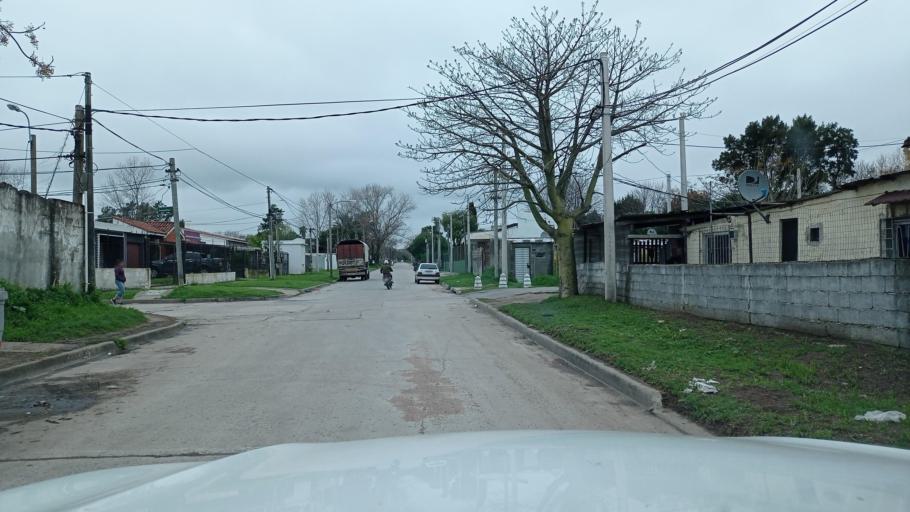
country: UY
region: Canelones
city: La Paz
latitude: -34.8396
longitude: -56.2366
